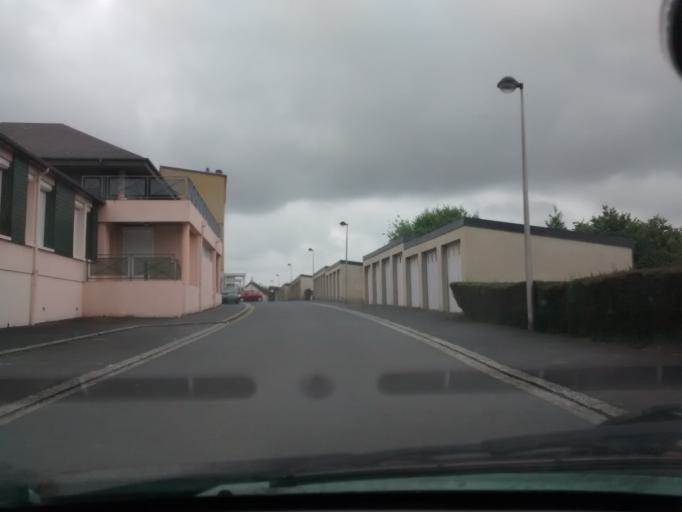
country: FR
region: Lower Normandy
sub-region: Departement de la Manche
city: Saint-Lo
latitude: 49.1099
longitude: -1.0848
